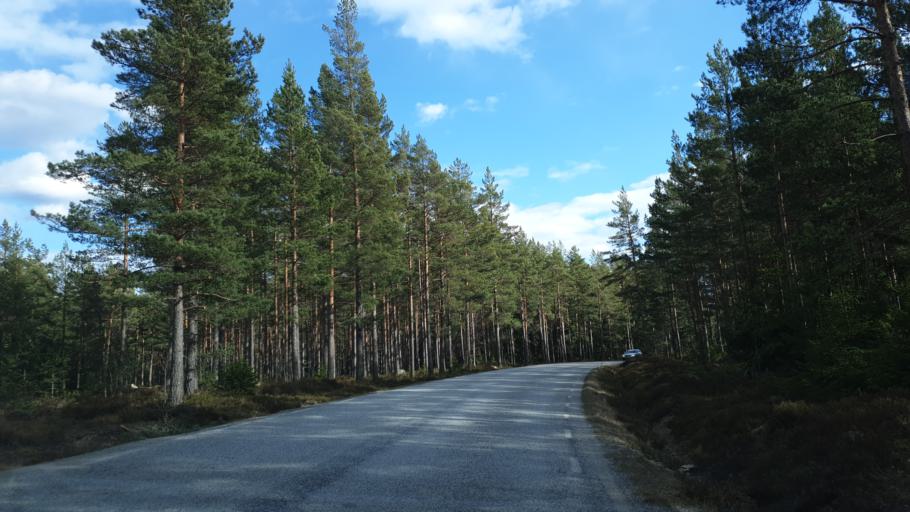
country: SE
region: Stockholm
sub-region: Varmdo Kommun
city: Mortnas
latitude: 59.2539
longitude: 18.4503
